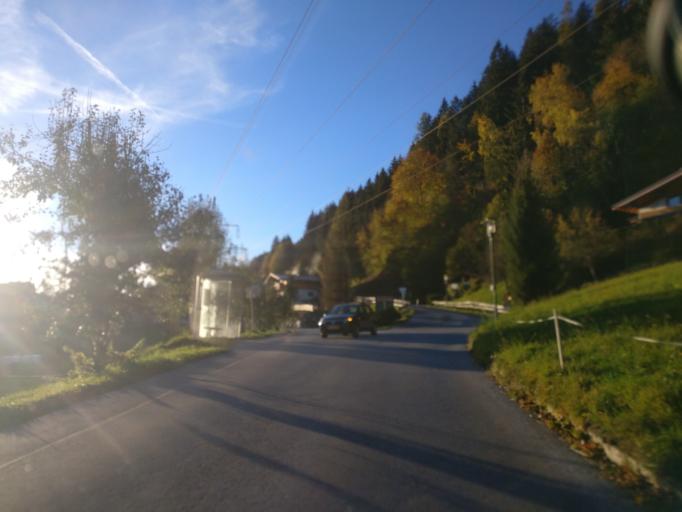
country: AT
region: Salzburg
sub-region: Politischer Bezirk Sankt Johann im Pongau
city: Sankt Veit im Pongau
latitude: 47.3338
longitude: 13.1498
